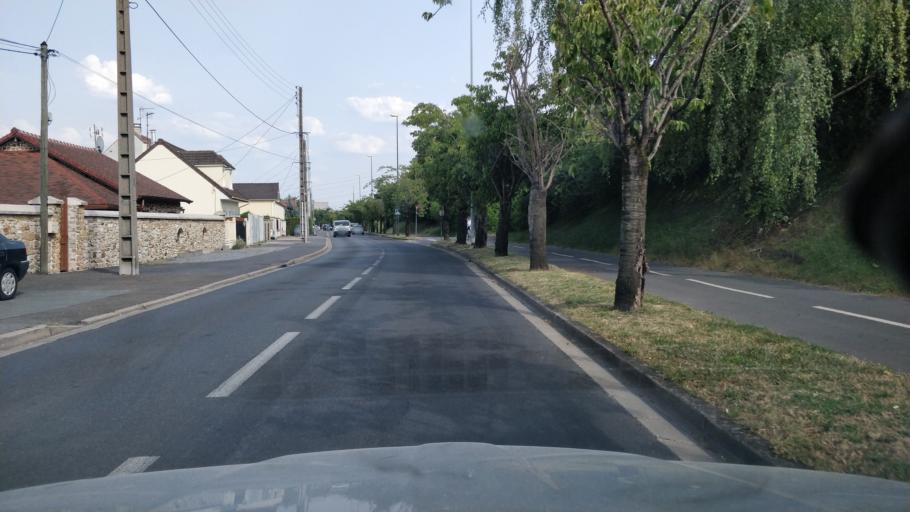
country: FR
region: Ile-de-France
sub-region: Departement de Seine-et-Marne
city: Chelles
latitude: 48.8890
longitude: 2.6085
